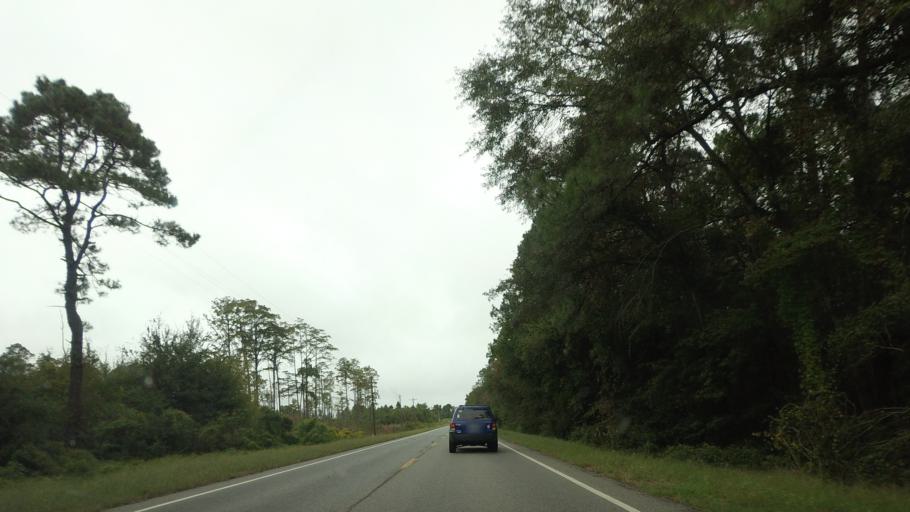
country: US
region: Georgia
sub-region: Irwin County
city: Ocilla
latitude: 31.5442
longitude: -83.2538
